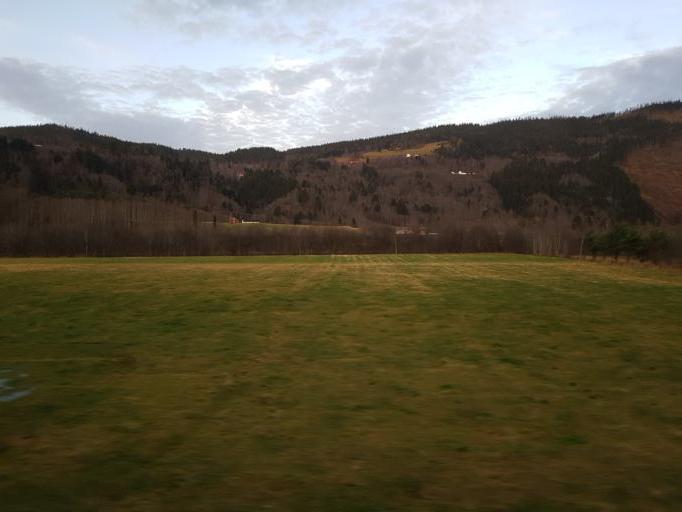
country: NO
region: Sor-Trondelag
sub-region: Melhus
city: Lundamo
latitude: 63.1291
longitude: 10.2478
